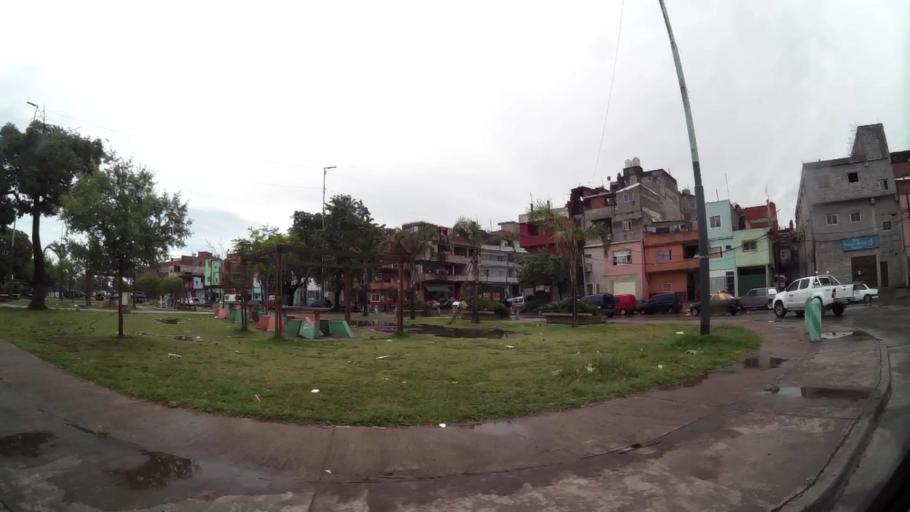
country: AR
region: Buenos Aires F.D.
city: Villa Lugano
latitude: -34.6510
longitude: -58.4429
